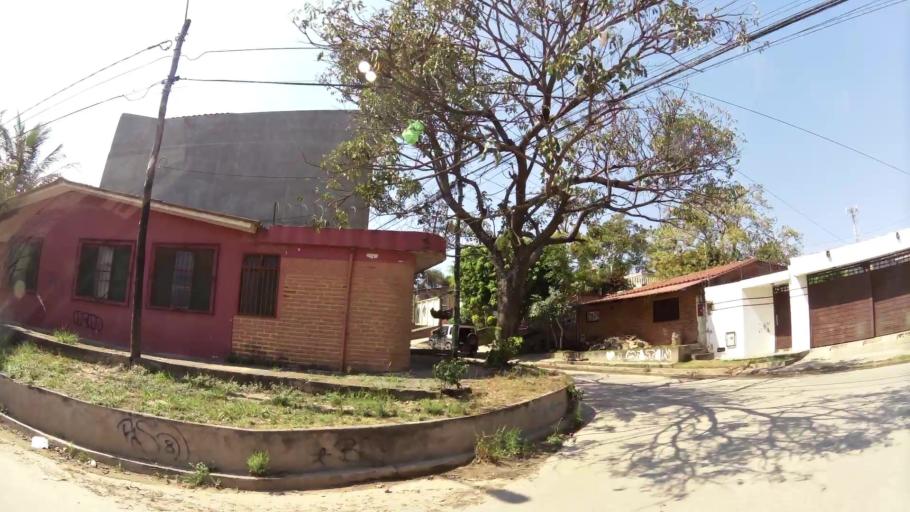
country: BO
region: Santa Cruz
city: Santa Cruz de la Sierra
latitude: -17.7445
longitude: -63.1806
